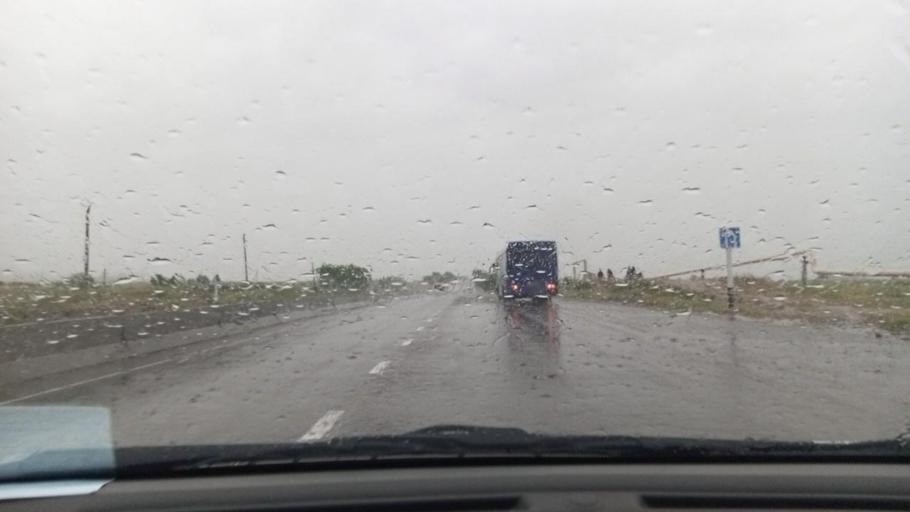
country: UZ
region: Toshkent
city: Angren
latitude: 40.9508
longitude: 69.9163
